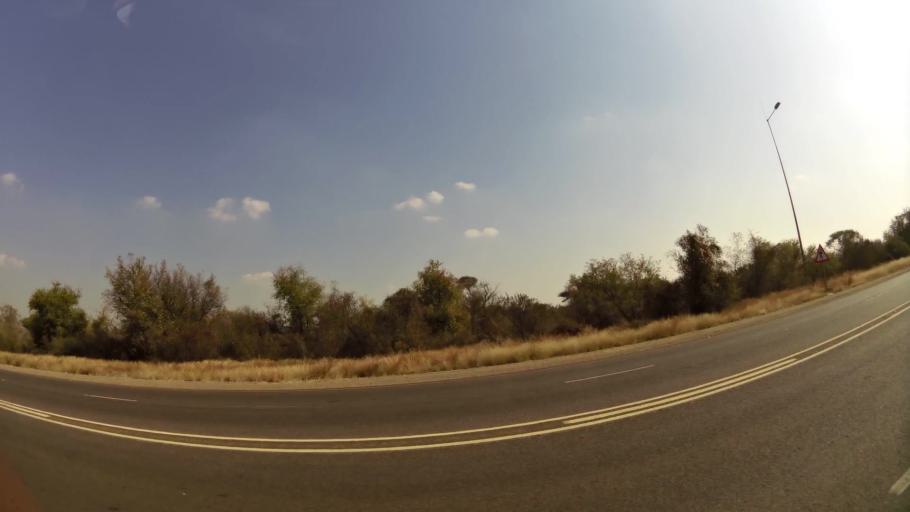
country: ZA
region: North-West
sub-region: Bojanala Platinum District Municipality
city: Mogwase
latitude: -25.4222
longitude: 27.0795
